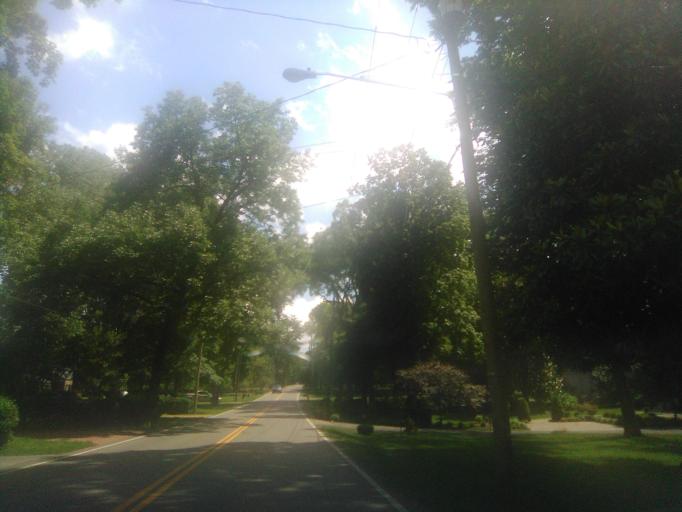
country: US
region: Tennessee
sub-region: Davidson County
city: Belle Meade
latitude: 36.1074
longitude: -86.8446
